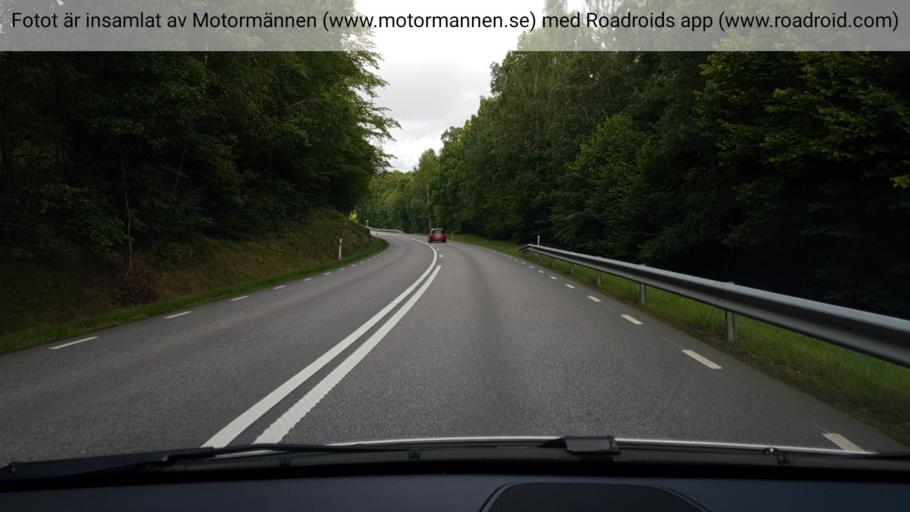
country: SE
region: Vaestra Goetaland
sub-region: Vargarda Kommun
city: Jonstorp
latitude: 58.0766
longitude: 12.6844
